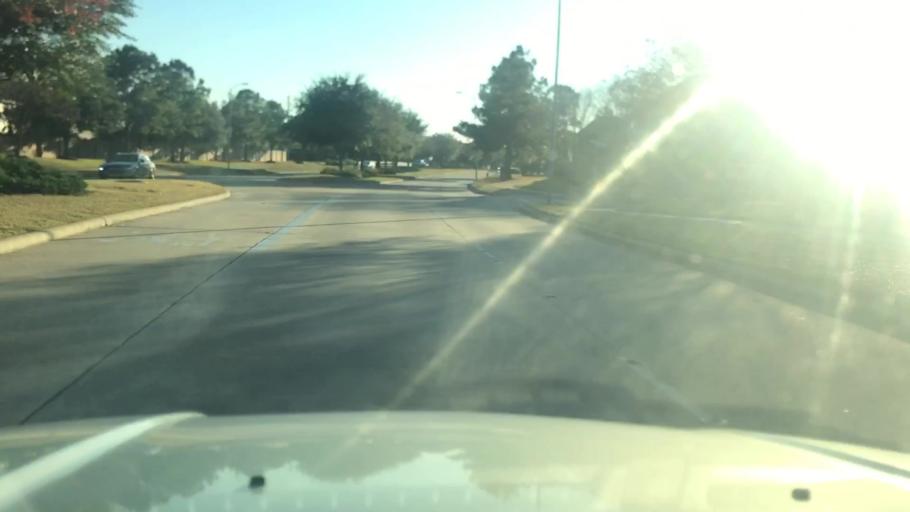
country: US
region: Texas
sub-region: Fort Bend County
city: Cinco Ranch
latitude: 29.7517
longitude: -95.7849
